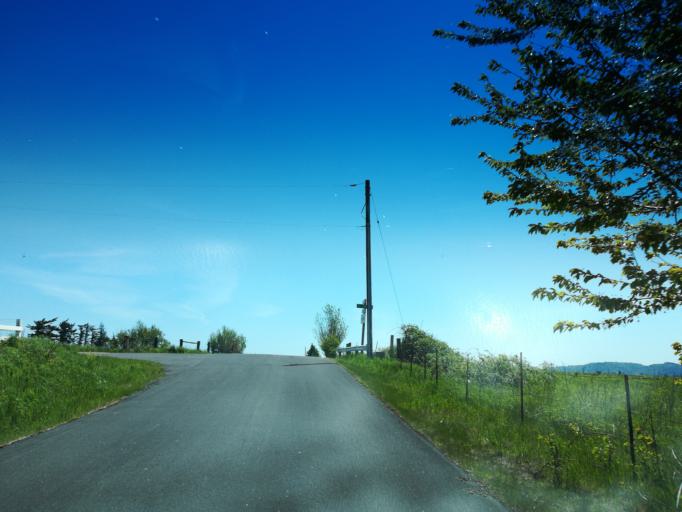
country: US
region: Oregon
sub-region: Multnomah County
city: Troutdale
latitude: 45.5337
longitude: -122.3625
